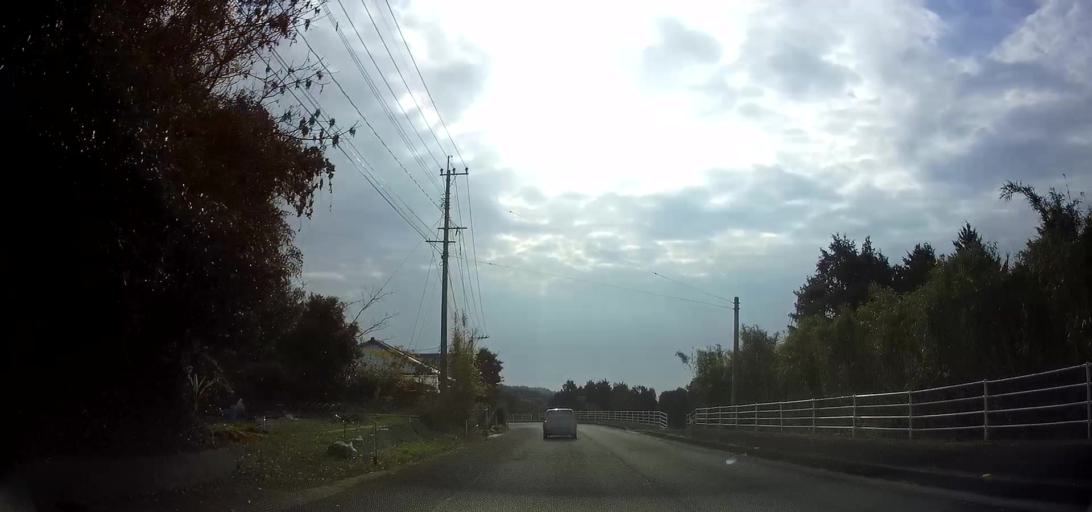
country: JP
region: Nagasaki
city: Shimabara
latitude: 32.6907
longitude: 130.2590
